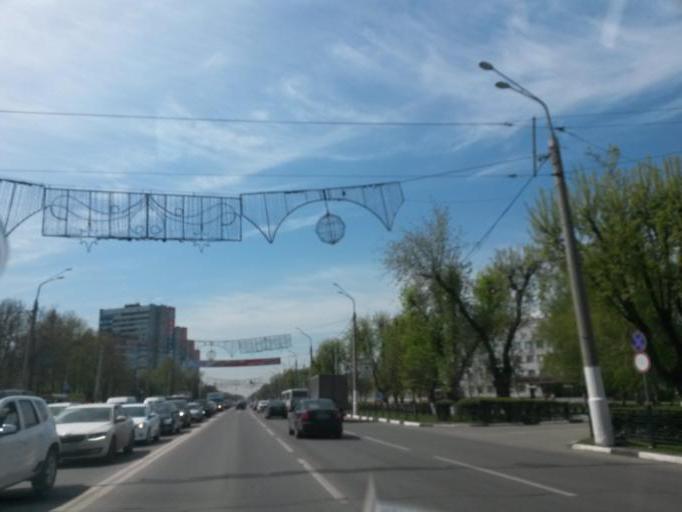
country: RU
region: Moskovskaya
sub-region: Podol'skiy Rayon
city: Podol'sk
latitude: 55.4307
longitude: 37.5445
